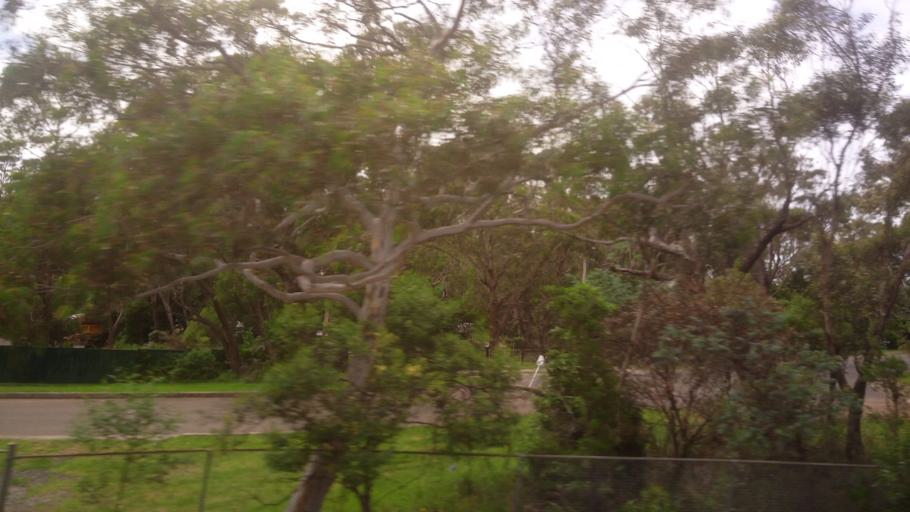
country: AU
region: New South Wales
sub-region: Blue Mountains Municipality
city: Leura
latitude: -33.7092
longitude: 150.3651
